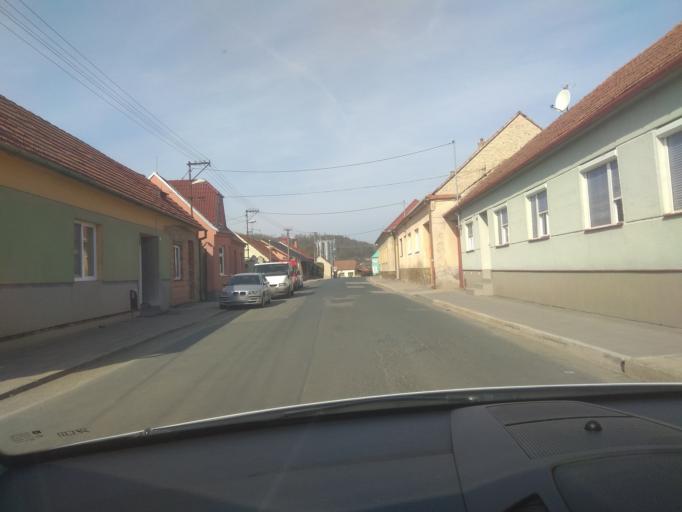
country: CZ
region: South Moravian
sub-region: Okres Brno-Venkov
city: Rosice
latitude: 49.1796
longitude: 16.3897
